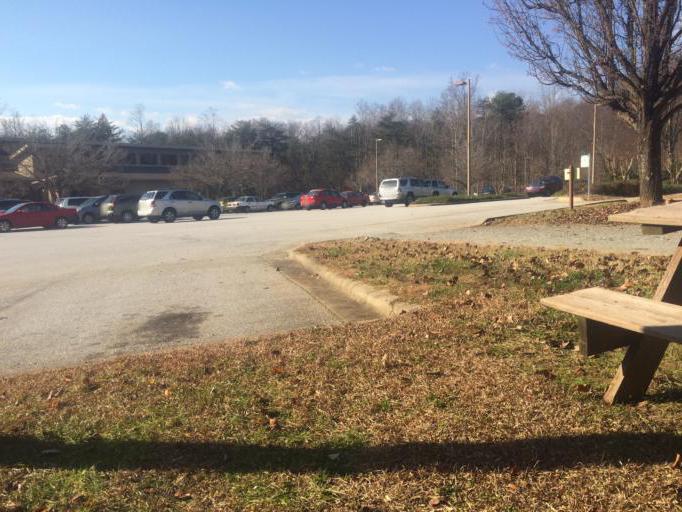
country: US
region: North Carolina
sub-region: Polk County
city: Columbus
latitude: 35.2398
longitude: -82.2167
